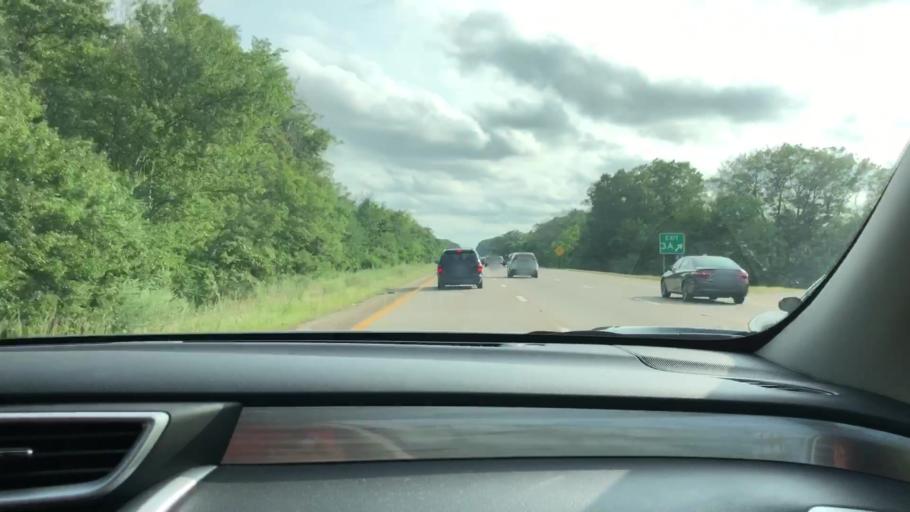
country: US
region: Massachusetts
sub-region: Bristol County
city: Attleboro
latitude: 41.9328
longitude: -71.3208
